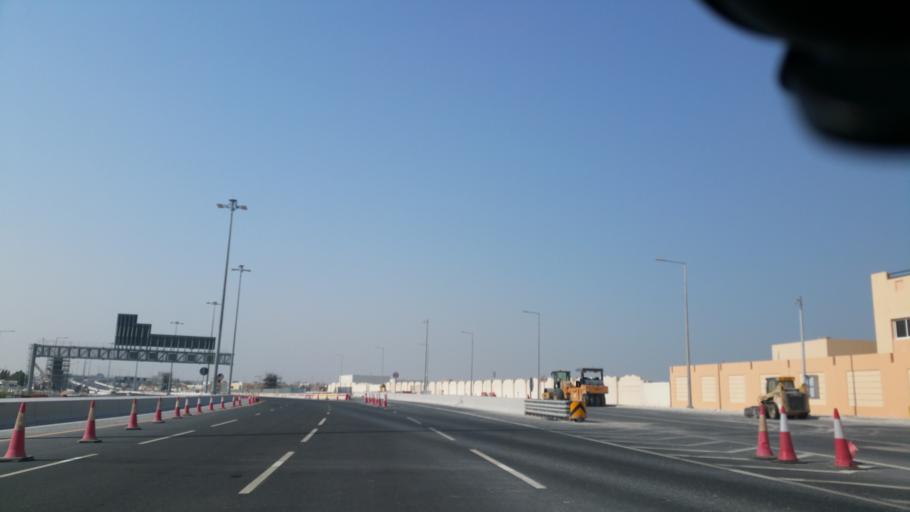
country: QA
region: Baladiyat ar Rayyan
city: Ar Rayyan
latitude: 25.3044
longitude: 51.4649
